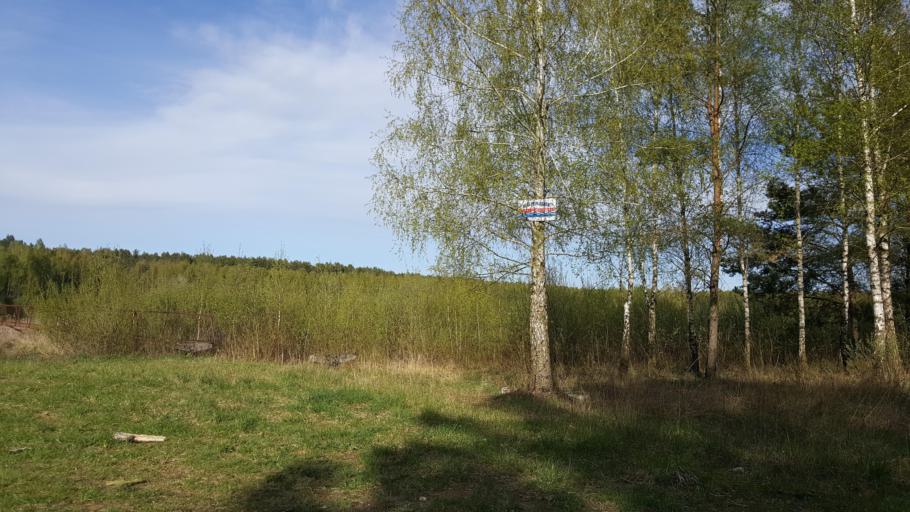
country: BY
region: Brest
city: Vysokaye
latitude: 52.4057
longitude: 23.4724
